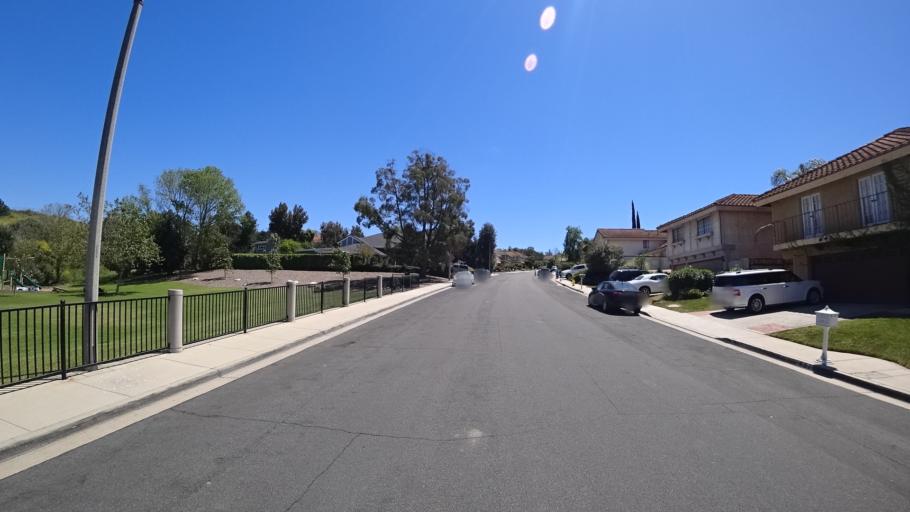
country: US
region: California
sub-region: Ventura County
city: Casa Conejo
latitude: 34.1836
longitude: -118.8972
